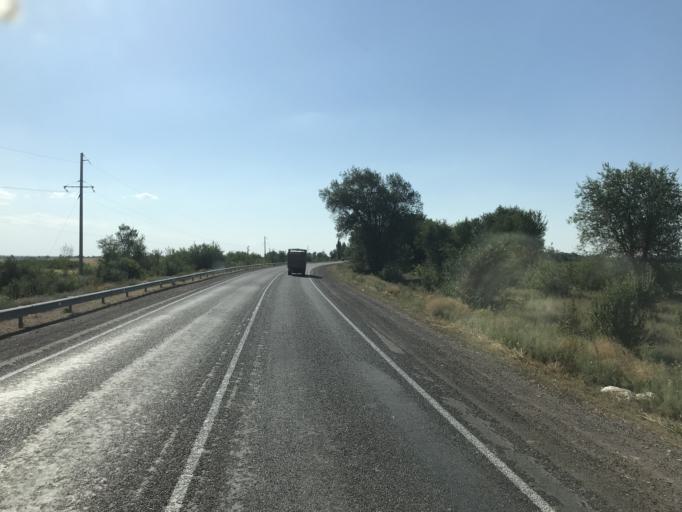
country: KZ
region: Zhambyl
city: Georgiyevka
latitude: 43.1906
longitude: 74.5416
